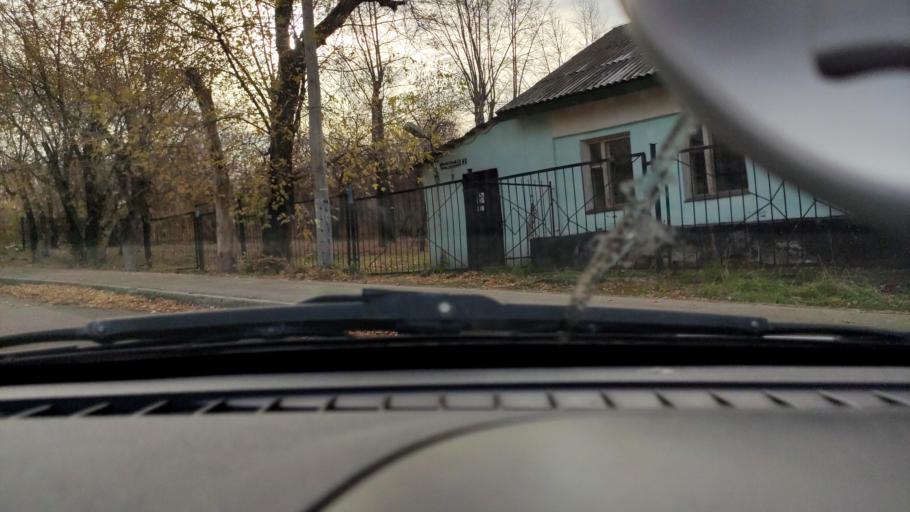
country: RU
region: Perm
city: Polazna
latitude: 58.1261
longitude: 56.3762
